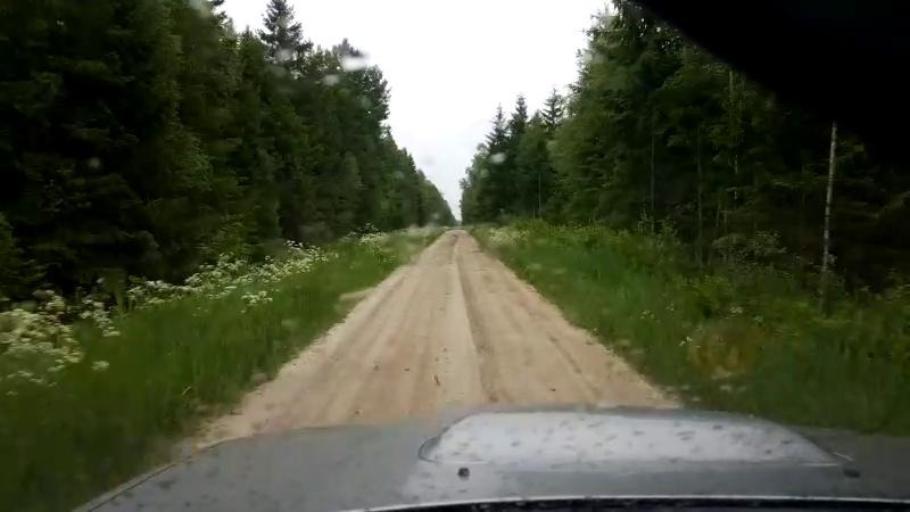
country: EE
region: Paernumaa
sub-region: Halinga vald
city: Parnu-Jaagupi
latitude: 58.5851
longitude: 24.6357
